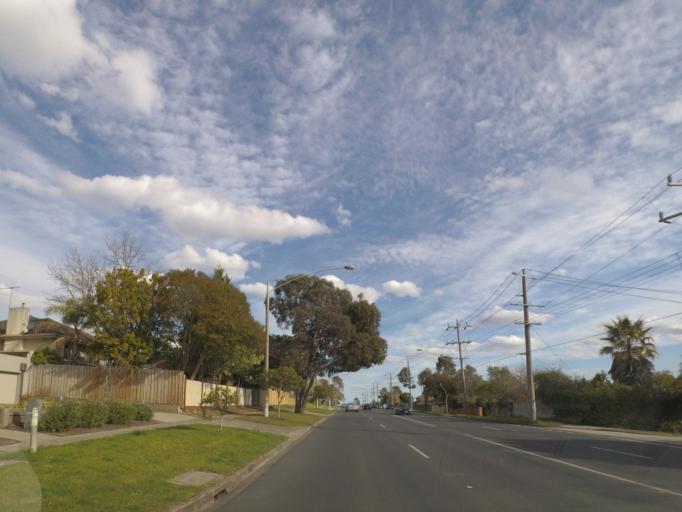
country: AU
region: Victoria
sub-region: Manningham
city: Doncaster East
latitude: -37.7921
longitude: 145.1429
